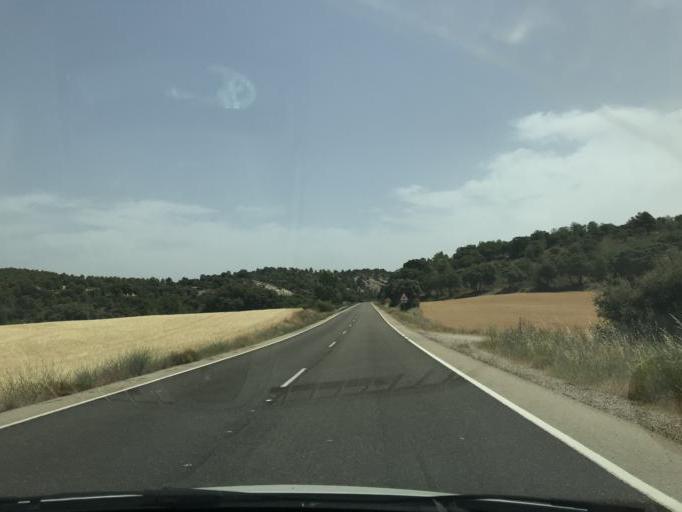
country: ES
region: Castille-La Mancha
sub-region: Provincia de Cuenca
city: La Frontera
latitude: 40.4001
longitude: -2.2508
